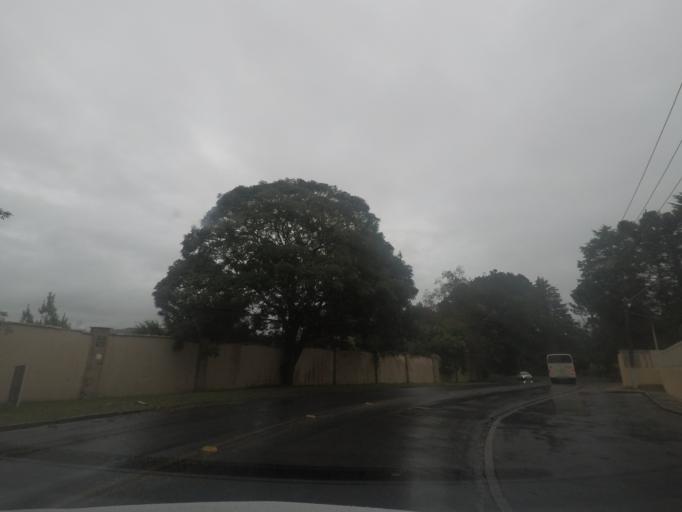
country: BR
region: Parana
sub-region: Quatro Barras
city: Quatro Barras
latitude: -25.3777
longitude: -49.1177
